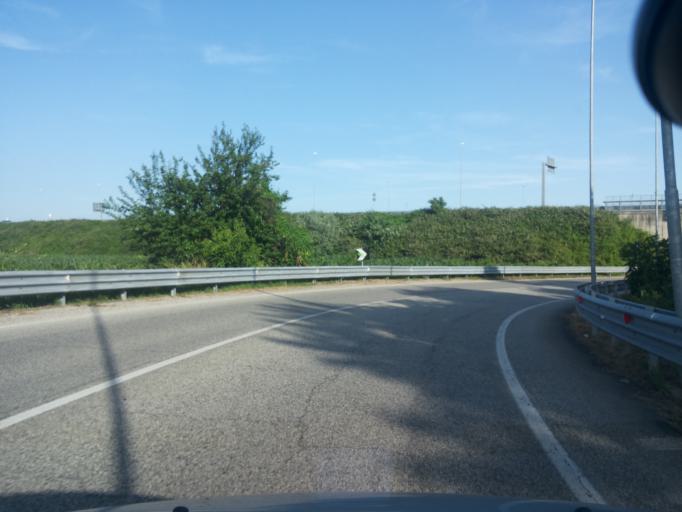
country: IT
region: Piedmont
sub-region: Provincia di Vercelli
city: Vercelli
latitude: 45.3420
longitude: 8.4287
